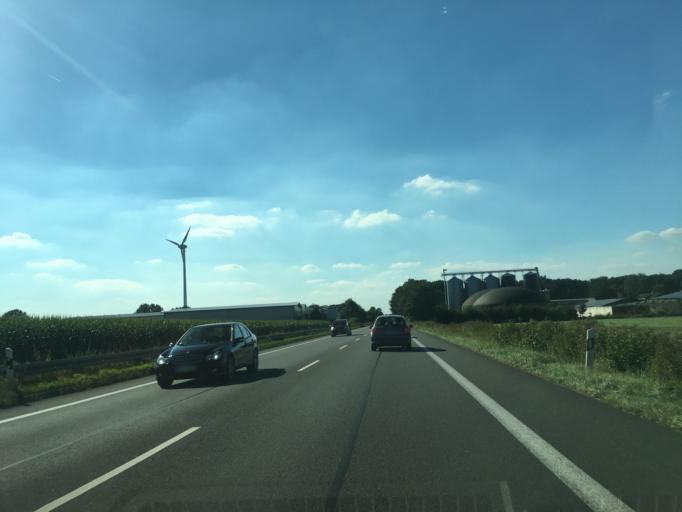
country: DE
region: North Rhine-Westphalia
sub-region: Regierungsbezirk Munster
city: Beelen
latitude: 51.9358
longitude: 8.0946
